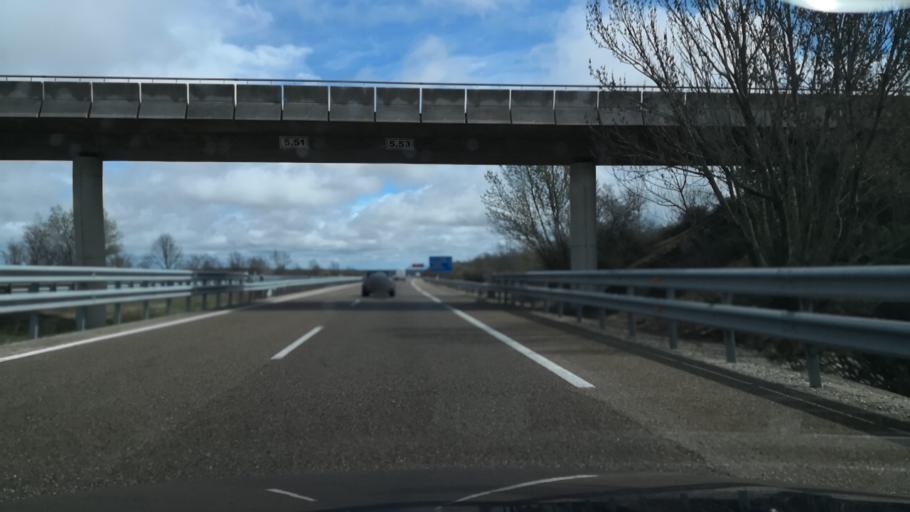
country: ES
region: Castille and Leon
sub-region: Provincia de Zamora
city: Mombuey
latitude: 42.0218
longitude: -6.3630
